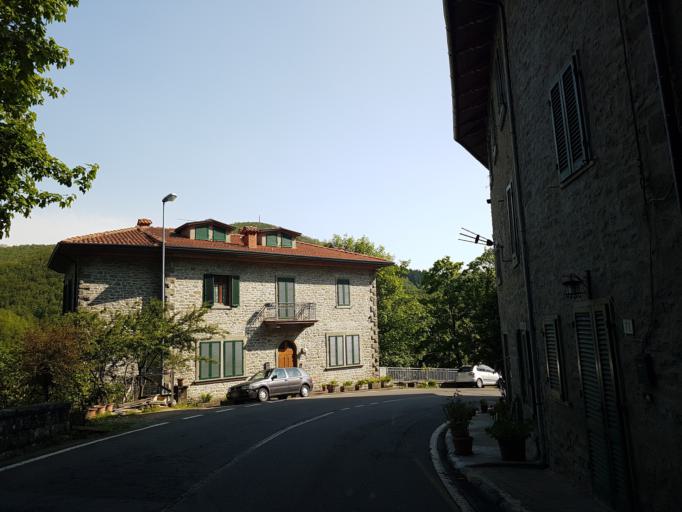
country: IT
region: Tuscany
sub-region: Province of Arezzo
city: Soci
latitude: 43.7941
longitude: 11.8817
